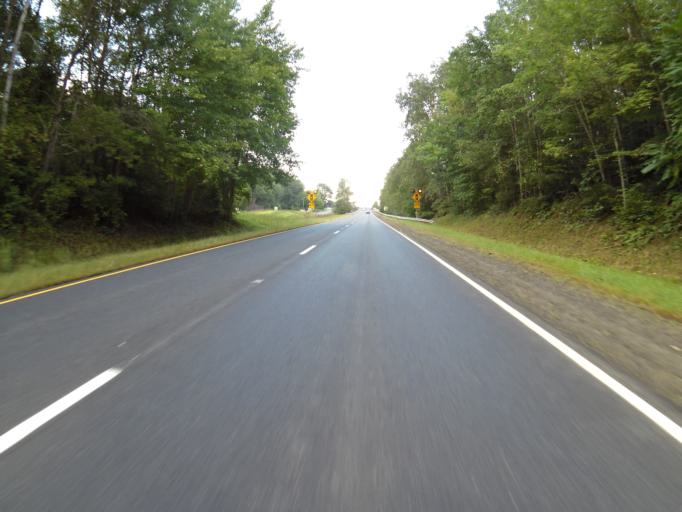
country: US
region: Virginia
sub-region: Fauquier County
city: Warrenton
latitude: 38.6765
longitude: -77.9231
